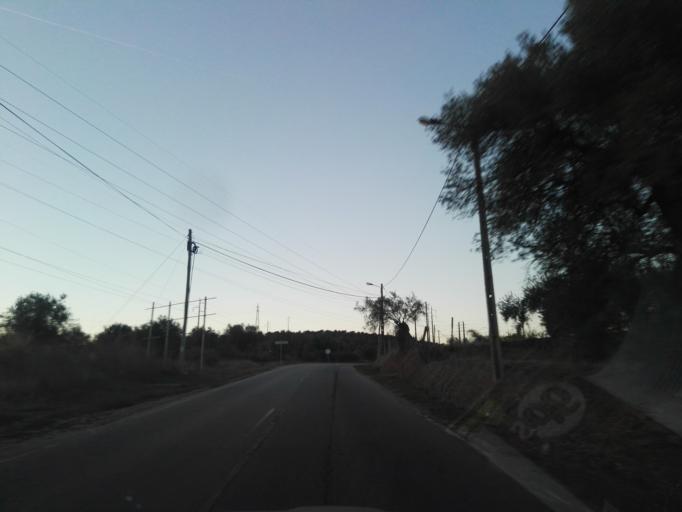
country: PT
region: Portalegre
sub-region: Elvas
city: Elvas
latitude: 38.8877
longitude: -7.1688
